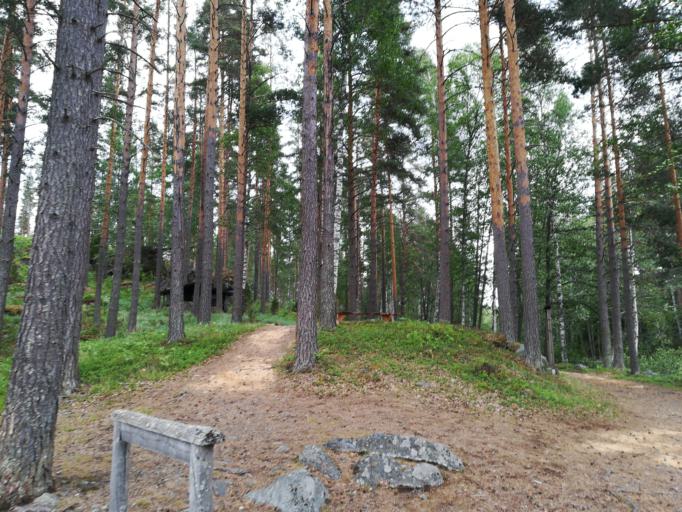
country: FI
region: South Karelia
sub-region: Lappeenranta
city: Savitaipale
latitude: 61.2576
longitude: 27.7089
